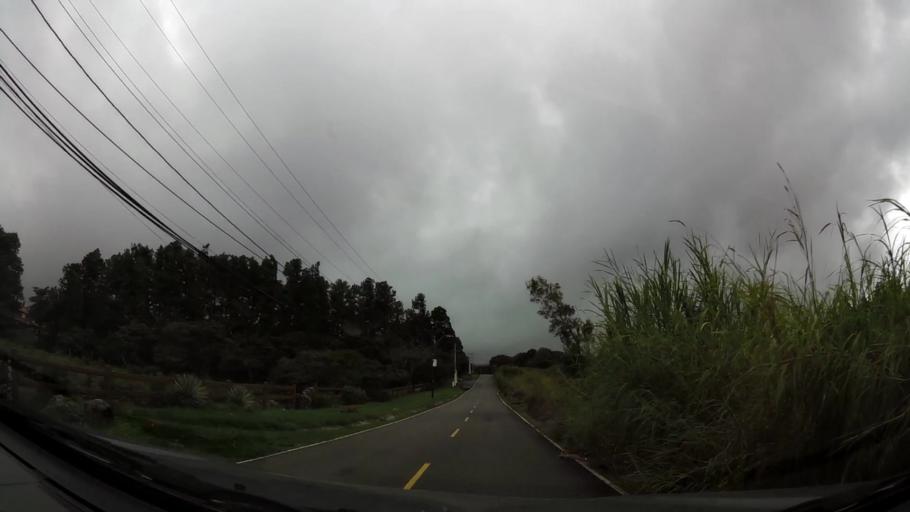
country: PA
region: Chiriqui
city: Palmira
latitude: 8.7396
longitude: -82.4414
